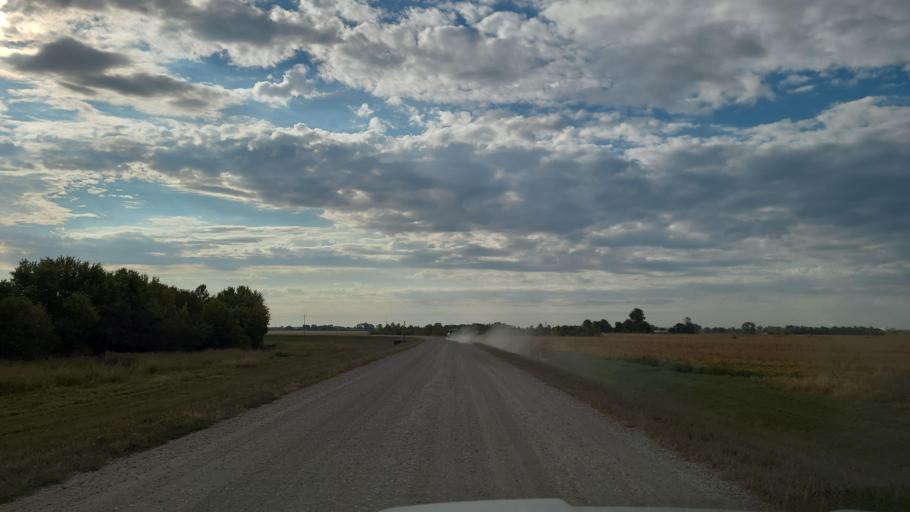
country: US
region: Kansas
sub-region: Douglas County
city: Lawrence
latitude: 39.0143
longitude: -95.2081
